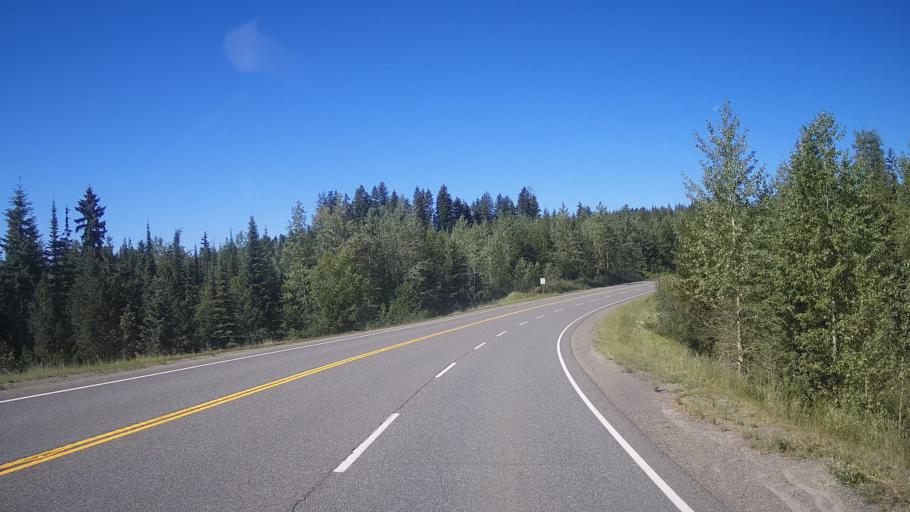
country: CA
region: British Columbia
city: Kamloops
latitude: 51.4875
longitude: -120.3147
